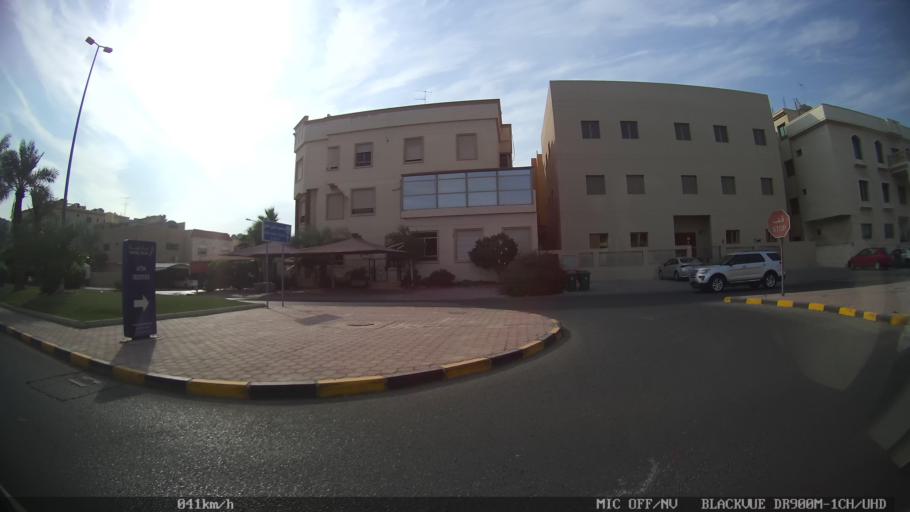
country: KW
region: Al Asimah
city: Ash Shamiyah
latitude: 29.3355
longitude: 47.9576
